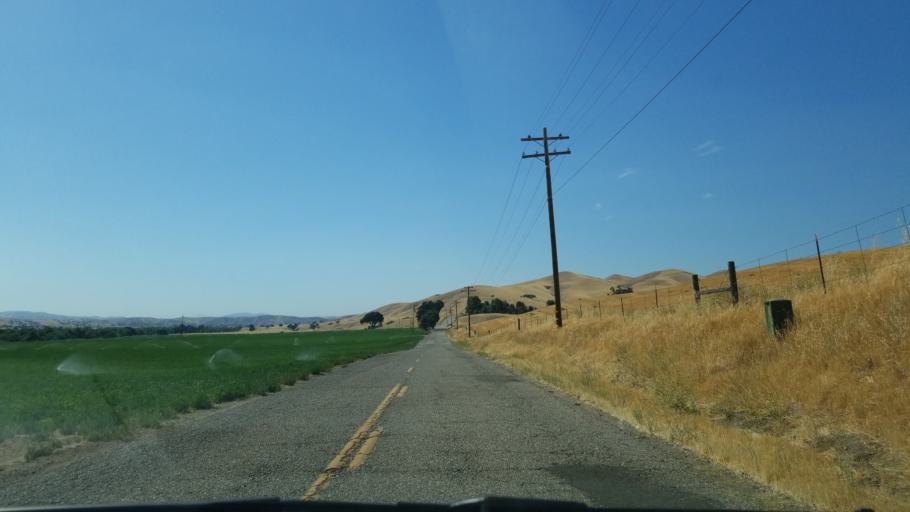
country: US
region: California
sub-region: San Luis Obispo County
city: San Miguel
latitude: 35.7696
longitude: -120.6893
